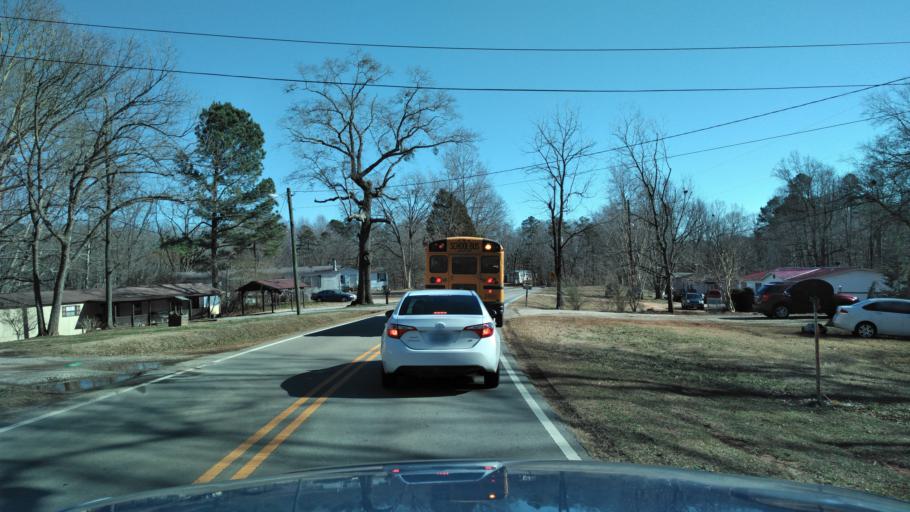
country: US
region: Georgia
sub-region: Hall County
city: Gainesville
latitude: 34.3169
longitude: -83.7556
